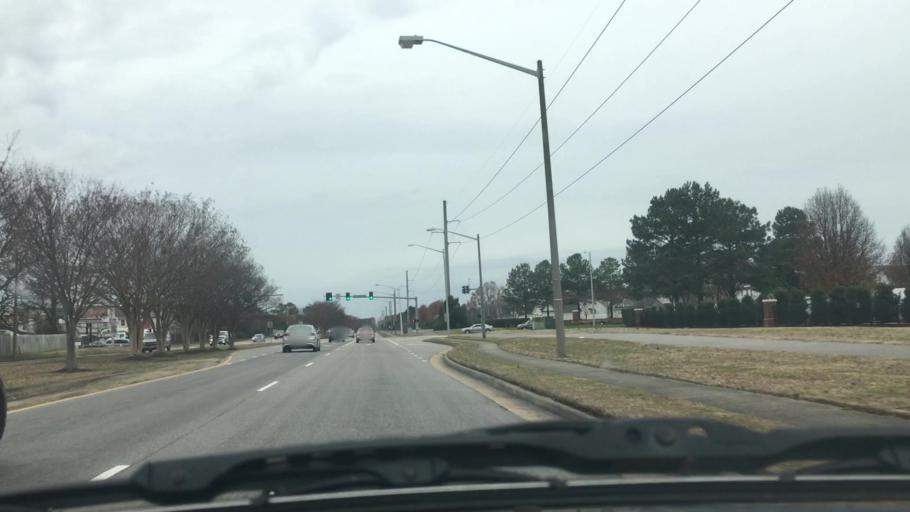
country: US
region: Virginia
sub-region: City of Virginia Beach
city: Virginia Beach
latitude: 36.8056
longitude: -76.1162
